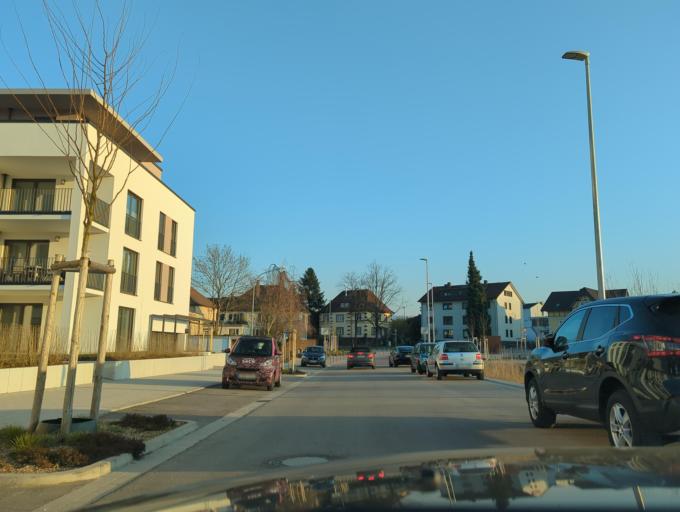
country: DE
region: Baden-Wuerttemberg
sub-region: Freiburg Region
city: Achern
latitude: 48.6295
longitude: 8.0662
